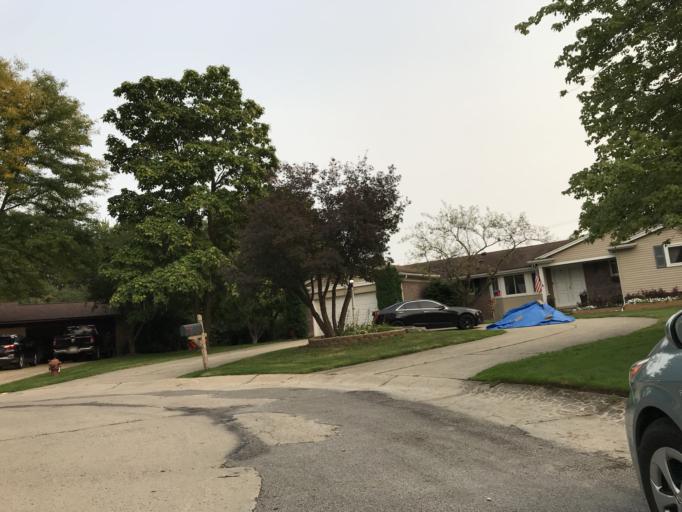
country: US
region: Michigan
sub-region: Oakland County
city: Franklin
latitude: 42.4844
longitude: -83.3244
